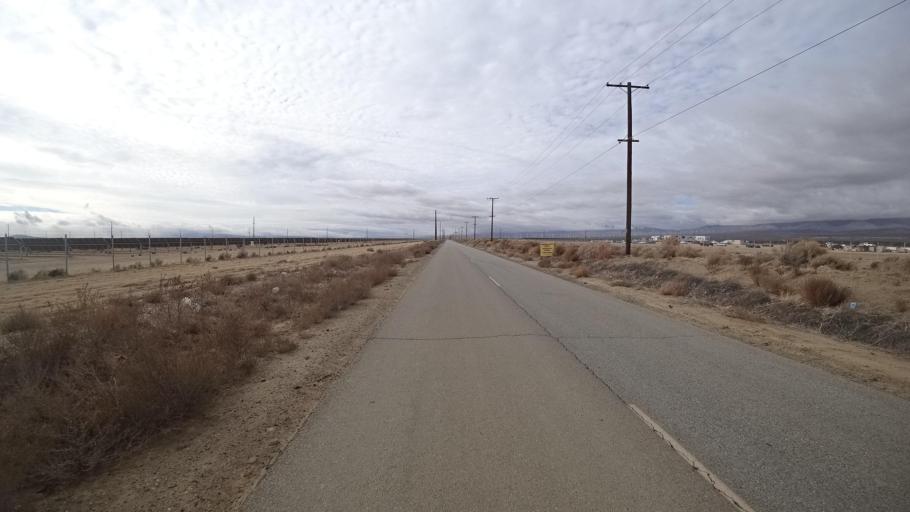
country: US
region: California
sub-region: Kern County
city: Rosamond
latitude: 34.8634
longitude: -118.3215
